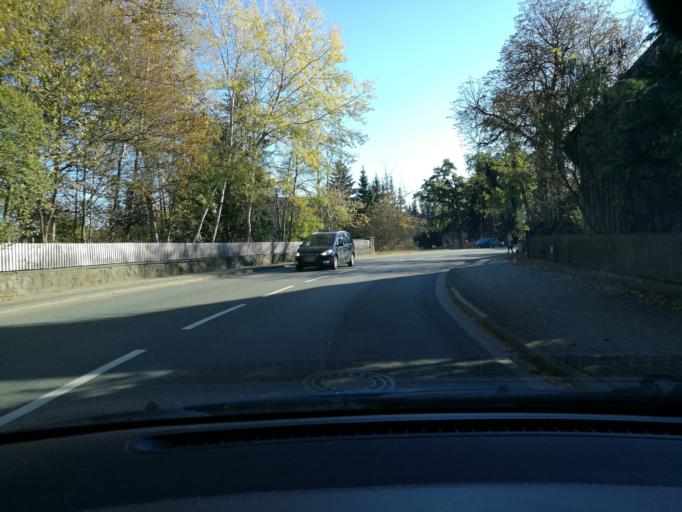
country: DE
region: Lower Saxony
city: Dannenberg
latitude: 53.0883
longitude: 11.0694
